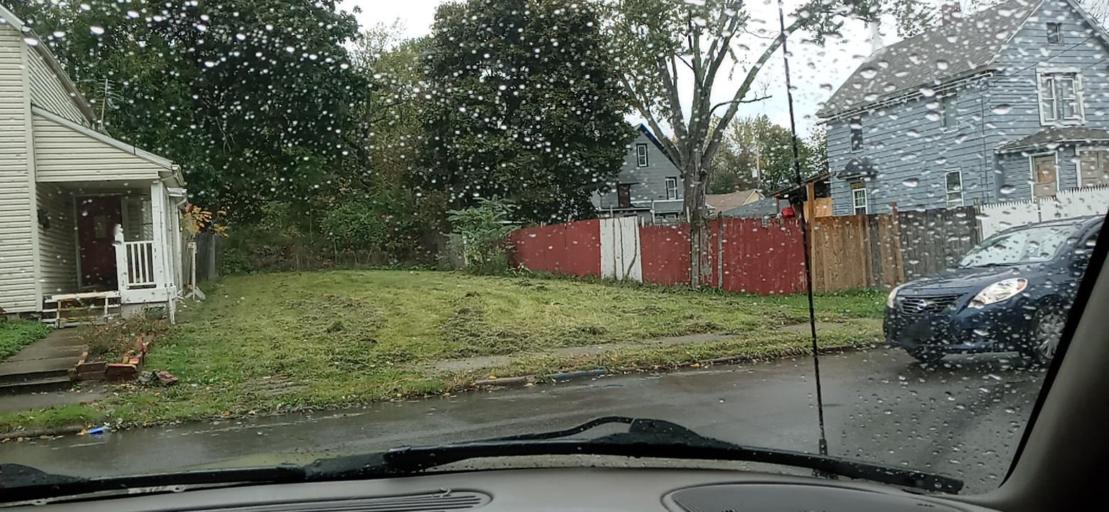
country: US
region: Ohio
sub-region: Summit County
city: Akron
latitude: 41.0596
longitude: -81.5312
